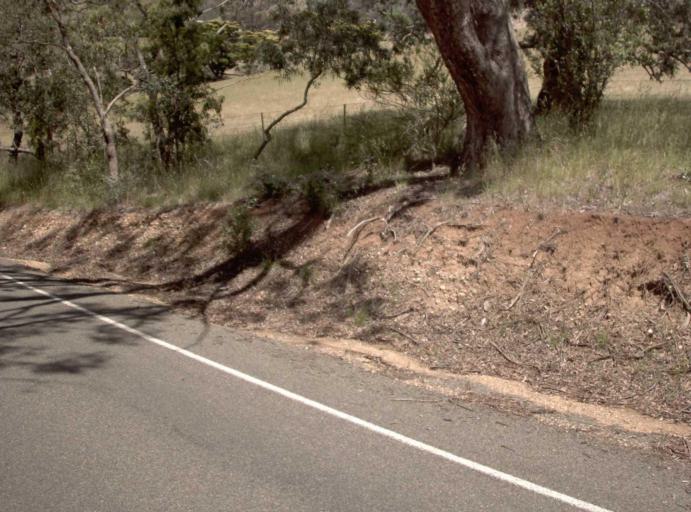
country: AU
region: Victoria
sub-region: East Gippsland
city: Bairnsdale
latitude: -37.4068
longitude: 147.8364
